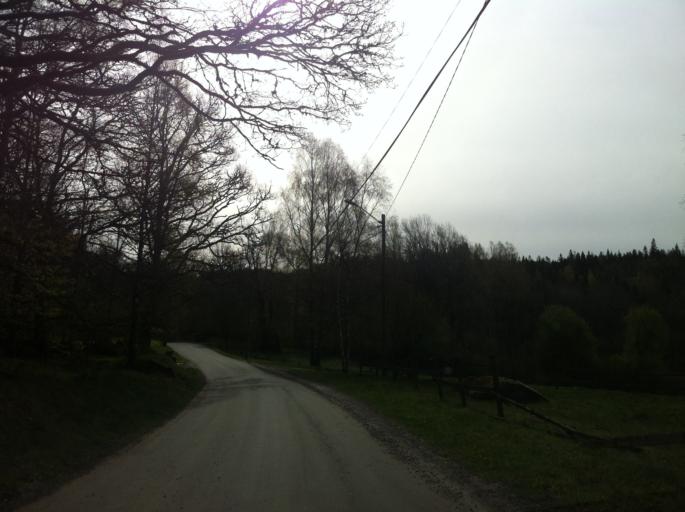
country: SE
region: Vaestra Goetaland
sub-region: Bollebygds Kommun
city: Bollebygd
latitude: 57.7517
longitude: 12.5969
